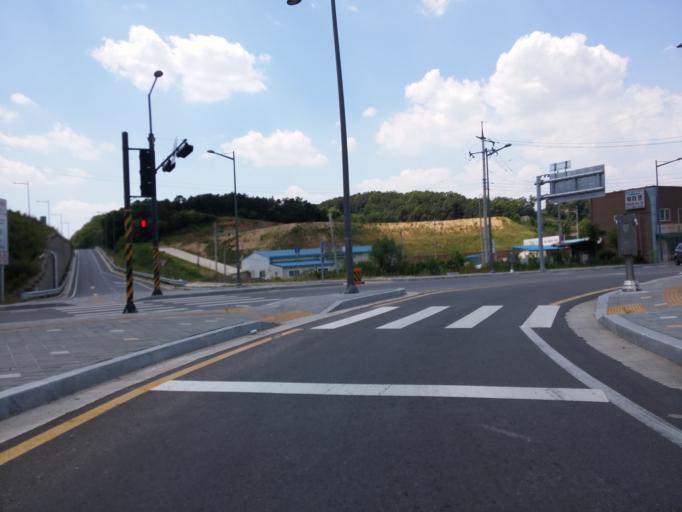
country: KR
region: Chungcheongbuk-do
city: Cheongju-si
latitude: 36.6031
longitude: 127.4407
